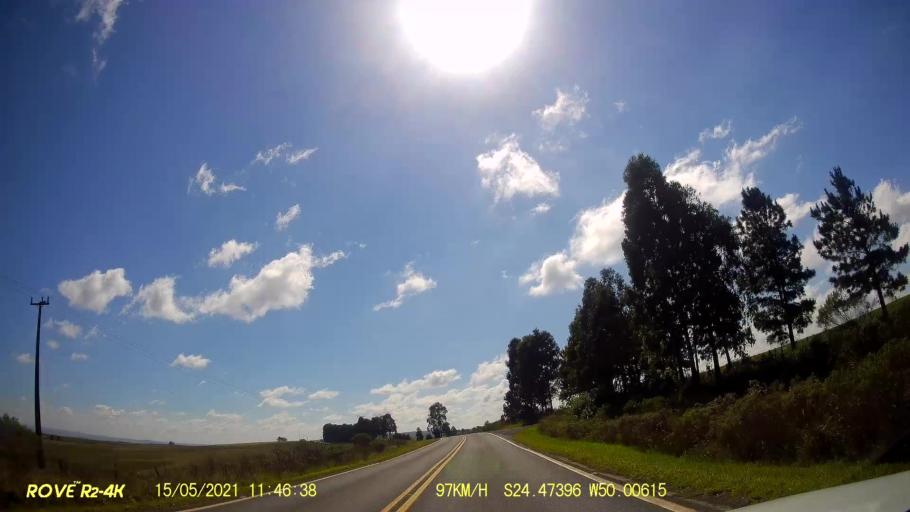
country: BR
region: Parana
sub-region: Pirai Do Sul
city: Pirai do Sul
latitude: -24.4740
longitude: -50.0061
